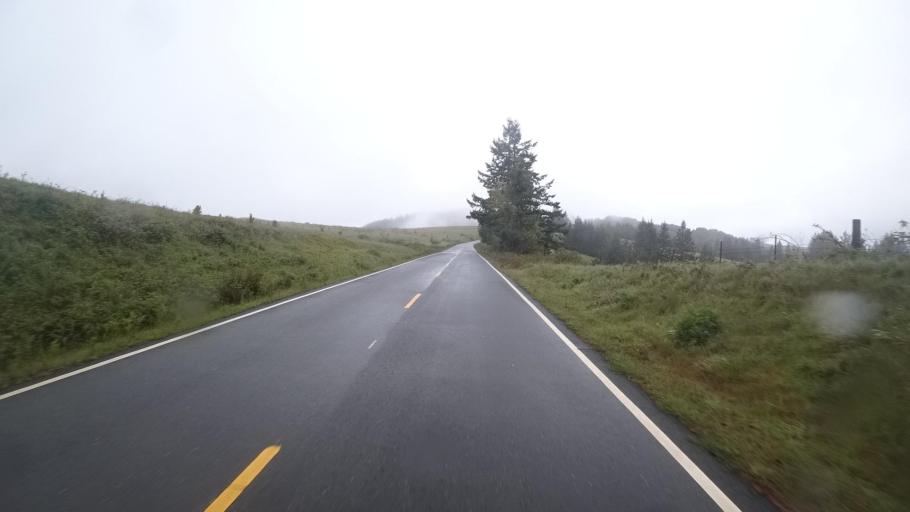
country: US
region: California
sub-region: Humboldt County
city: Westhaven-Moonstone
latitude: 41.1704
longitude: -123.9189
